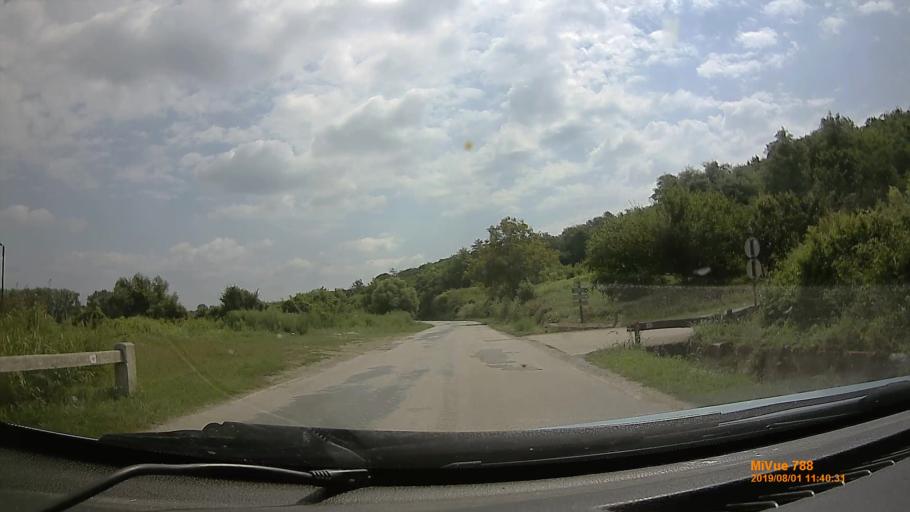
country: HU
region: Baranya
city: Villany
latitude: 45.8909
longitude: 18.3950
